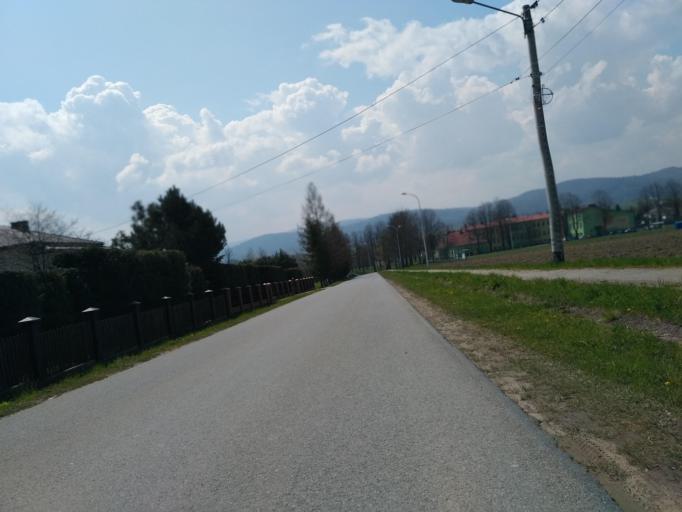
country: PL
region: Subcarpathian Voivodeship
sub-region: Powiat sanocki
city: Zarszyn
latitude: 49.5467
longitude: 21.9796
